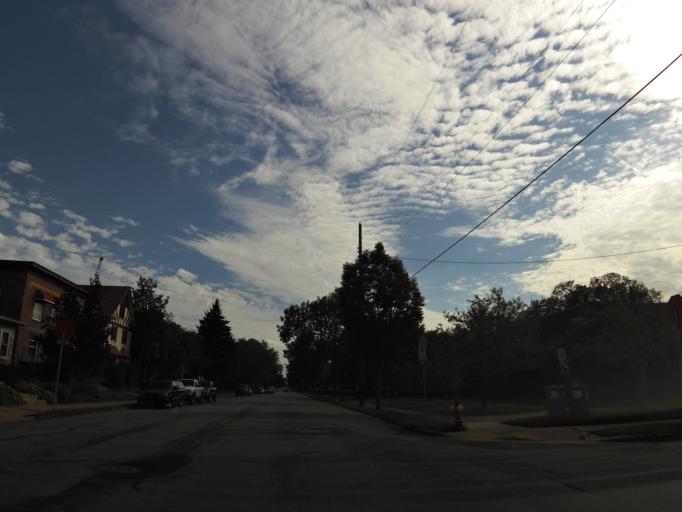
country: US
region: Minnesota
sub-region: Hennepin County
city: Minneapolis
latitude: 45.0010
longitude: -93.2525
